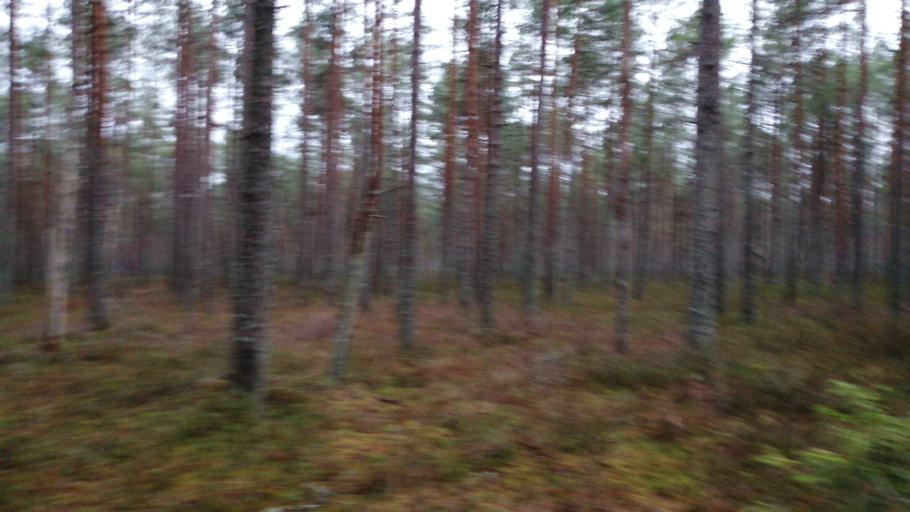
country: EE
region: Polvamaa
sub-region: Polva linn
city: Polva
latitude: 58.1548
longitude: 27.0634
